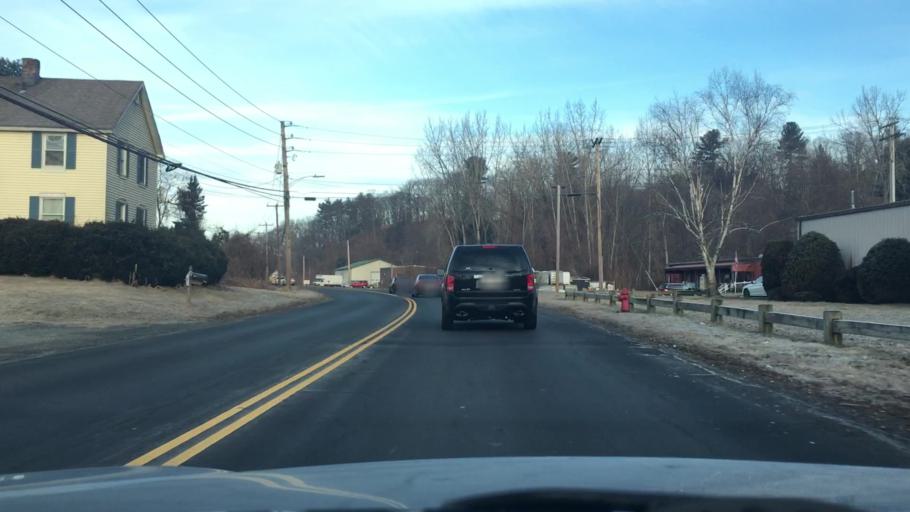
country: US
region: Massachusetts
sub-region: Hampden County
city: Westfield
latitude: 42.1211
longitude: -72.7164
